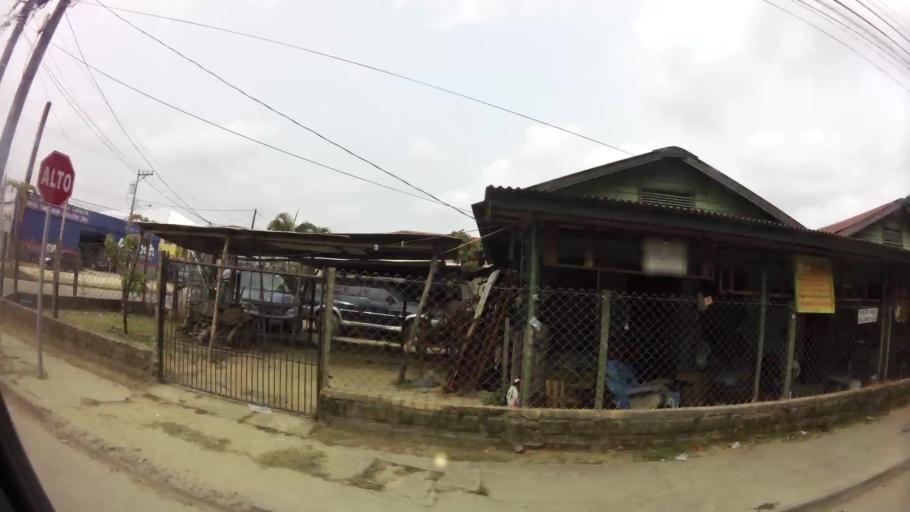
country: HN
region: Atlantida
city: Tela
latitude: 15.7806
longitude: -87.4516
